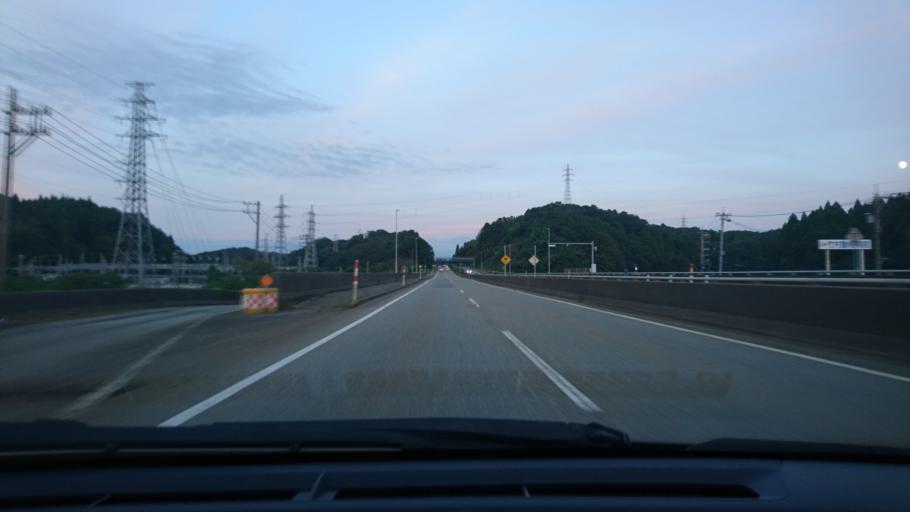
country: JP
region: Fukui
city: Maruoka
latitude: 36.2986
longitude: 136.3225
